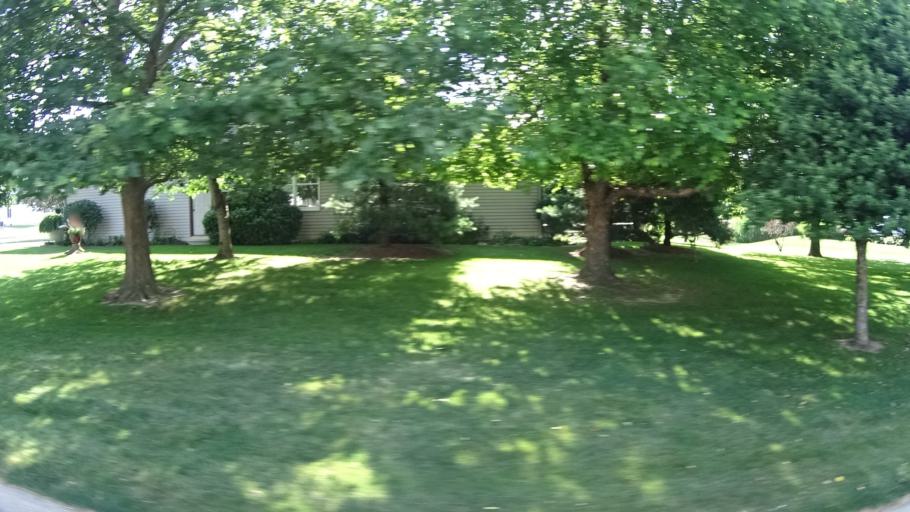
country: US
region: Ohio
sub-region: Erie County
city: Huron
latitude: 41.3837
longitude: -82.5215
